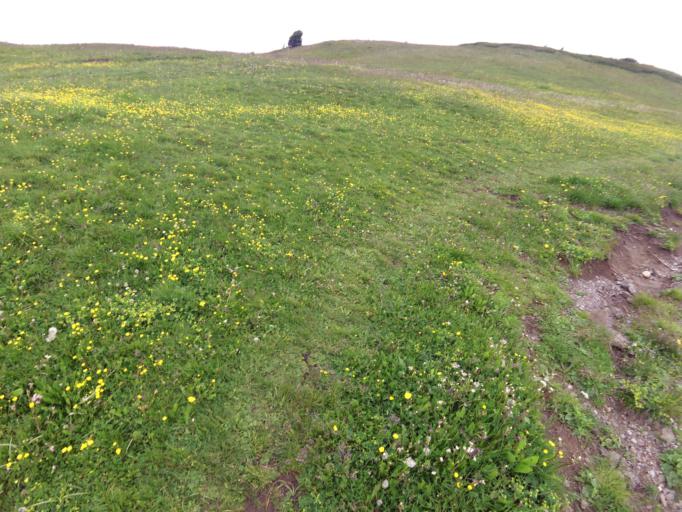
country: IT
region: Trentino-Alto Adige
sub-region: Bolzano
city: Castelrotto
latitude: 46.5500
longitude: 11.6151
